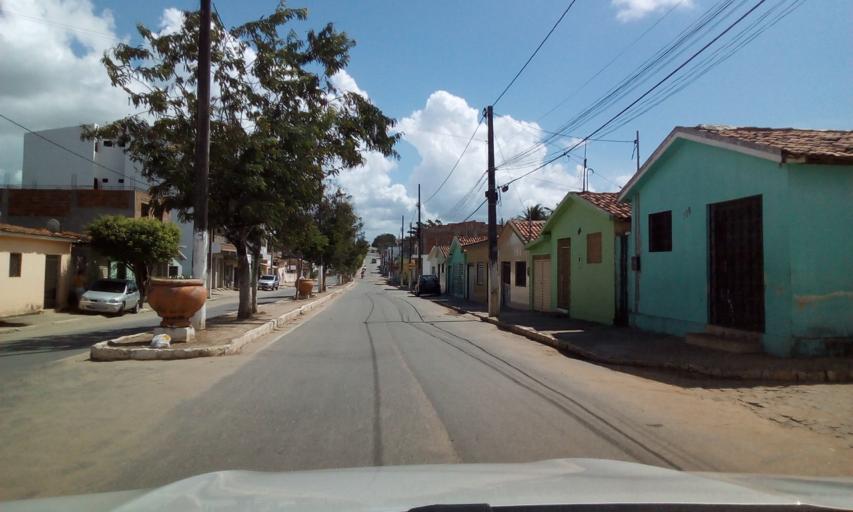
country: BR
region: Paraiba
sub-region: Guarabira
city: Guarabira
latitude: -6.8514
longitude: -35.3837
